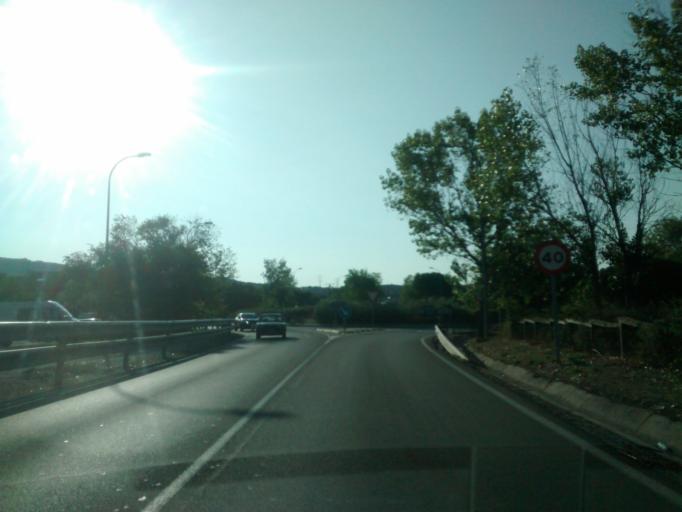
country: ES
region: Madrid
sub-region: Provincia de Madrid
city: Collado-Villalba
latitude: 40.6516
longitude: -4.0011
